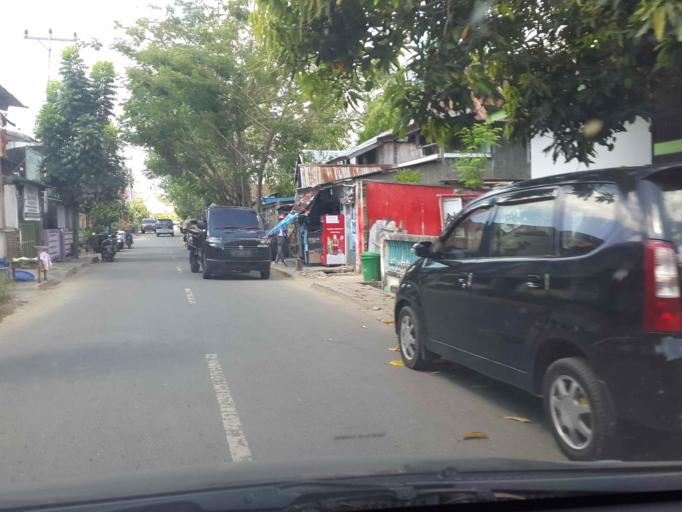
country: ID
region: South Sulawesi
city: Bantaeng
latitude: -6.1218
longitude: 120.4578
